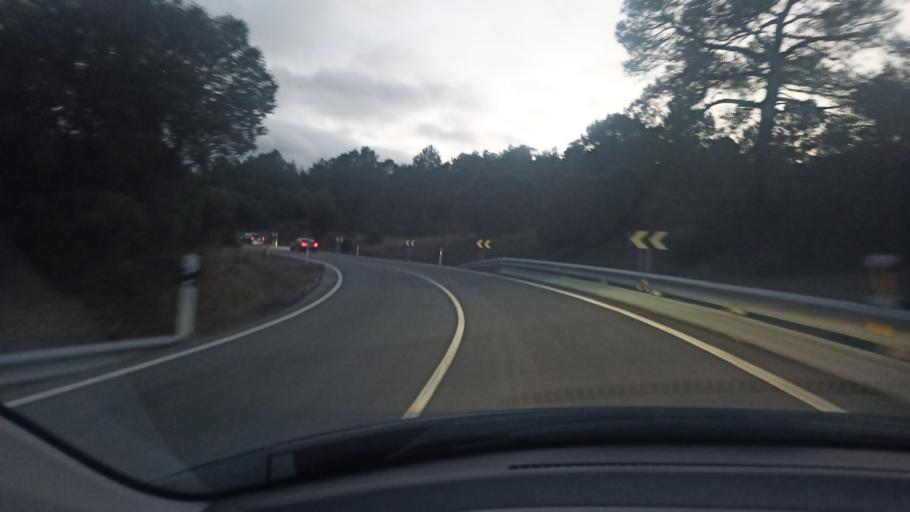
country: ES
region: Madrid
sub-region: Provincia de Madrid
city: Robledo de Chavela
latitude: 40.4638
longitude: -4.2607
